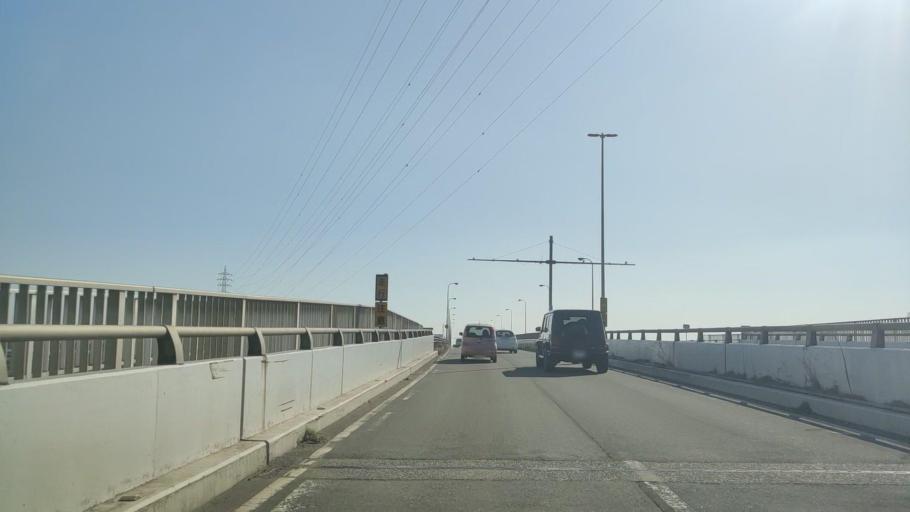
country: JP
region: Gifu
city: Gifu-shi
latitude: 35.4212
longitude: 136.7284
